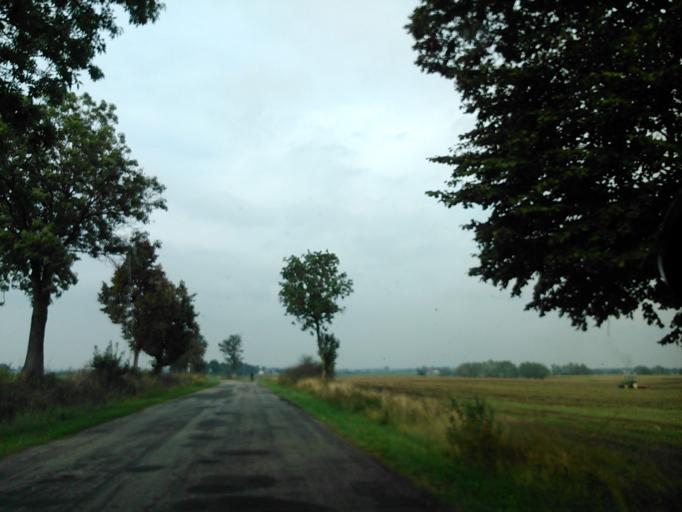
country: PL
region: Kujawsko-Pomorskie
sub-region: Powiat wabrzeski
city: Pluznica
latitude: 53.2401
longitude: 18.8183
